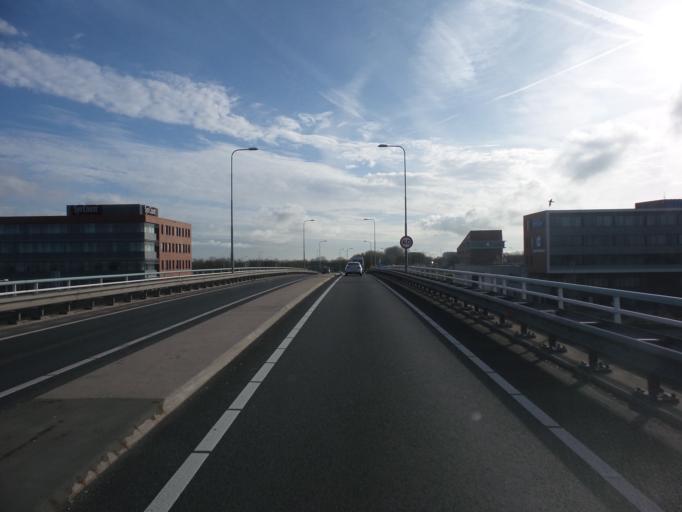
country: NL
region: South Holland
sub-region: Bodegraven-Reeuwijk
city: Bodegraven
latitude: 52.0878
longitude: 4.7348
